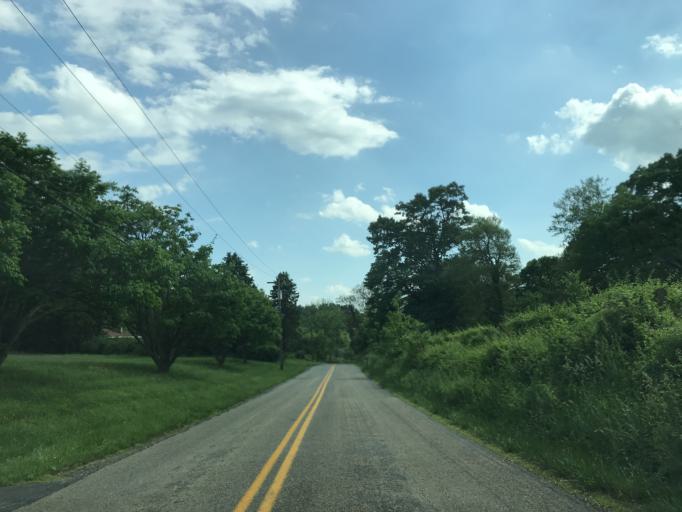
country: US
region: Pennsylvania
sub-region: York County
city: Susquehanna Trails
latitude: 39.6650
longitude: -76.3734
